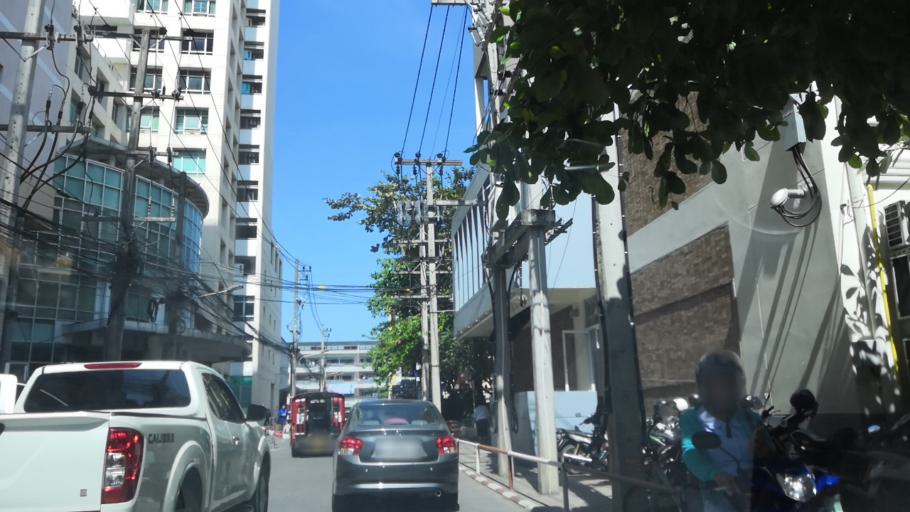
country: TH
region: Chiang Mai
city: Chiang Mai
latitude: 18.7893
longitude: 98.9754
